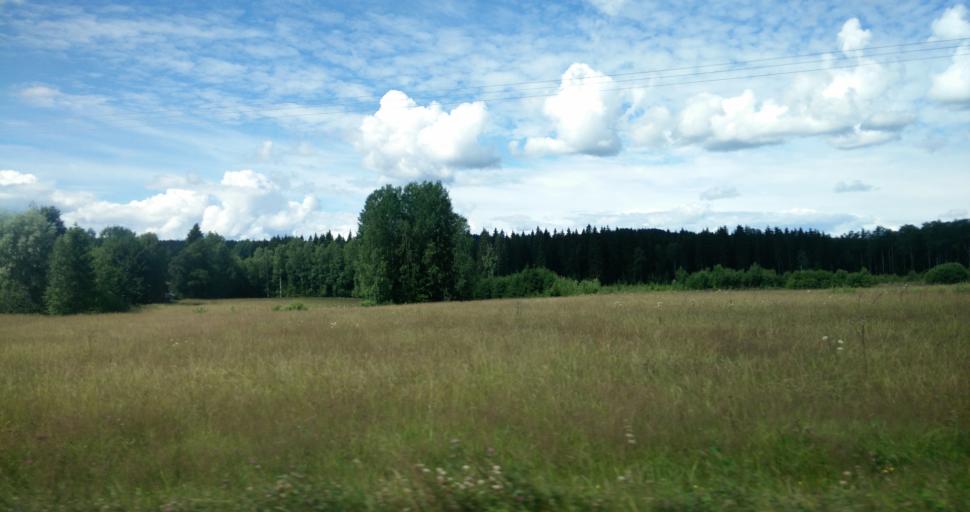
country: SE
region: Vaermland
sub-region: Hagfors Kommun
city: Ekshaerad
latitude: 60.1049
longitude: 13.4512
